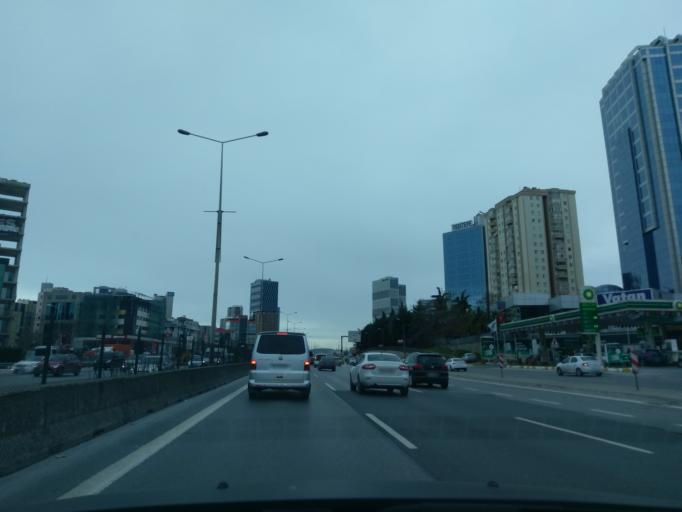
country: TR
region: Istanbul
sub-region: Atasehir
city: Atasehir
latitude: 40.9665
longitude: 29.1041
